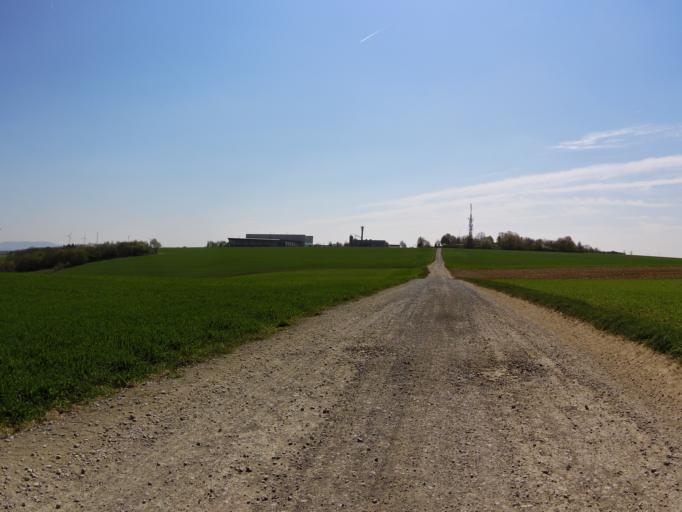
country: DE
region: Bavaria
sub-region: Regierungsbezirk Unterfranken
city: Biebelried
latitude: 49.7873
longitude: 10.0643
